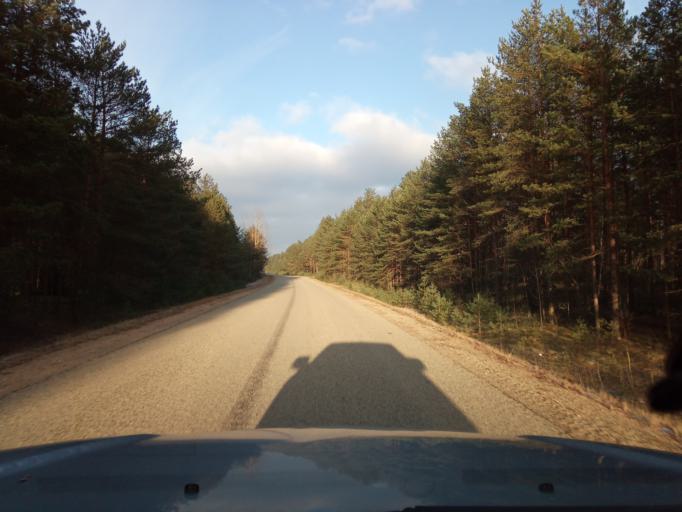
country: LT
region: Alytaus apskritis
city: Varena
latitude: 54.1663
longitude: 24.5053
